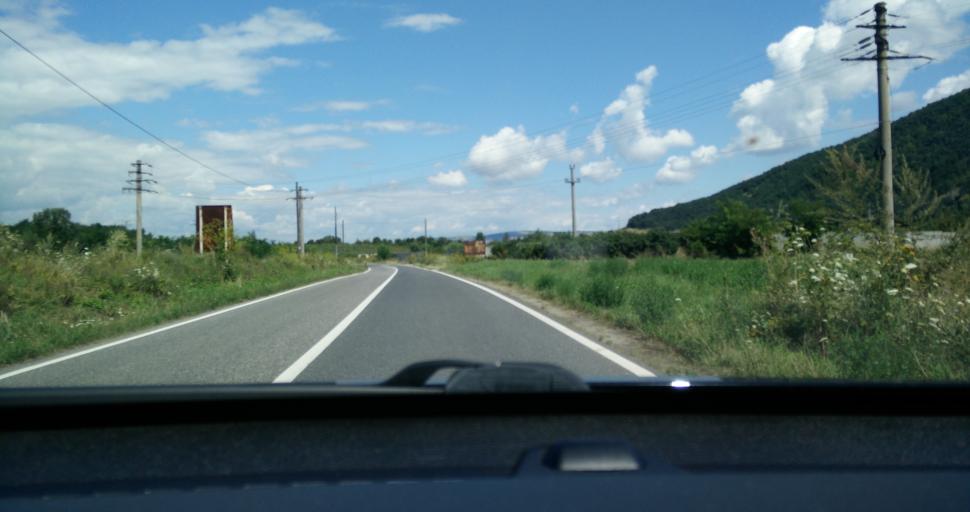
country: RO
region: Alba
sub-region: Comuna Sasciori
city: Sebesel
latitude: 45.8964
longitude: 23.5601
